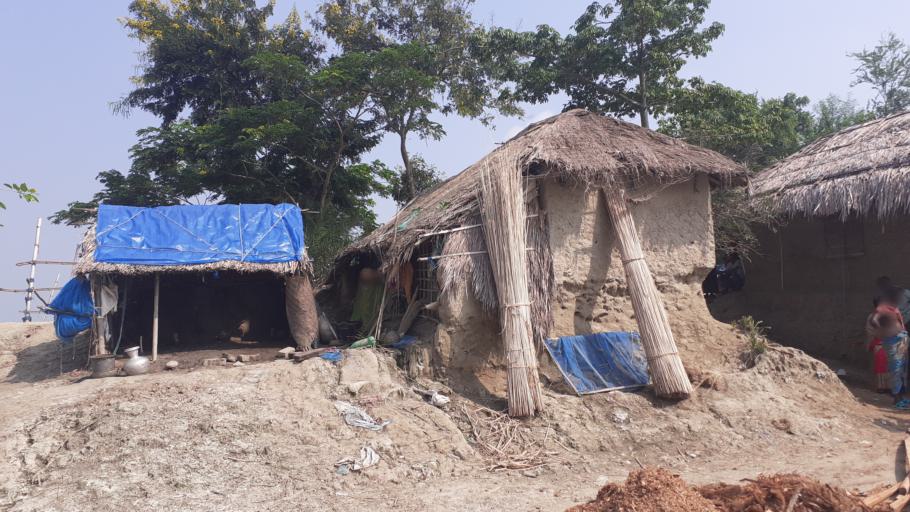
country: BD
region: Khulna
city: Phultala
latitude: 22.6613
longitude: 89.3981
